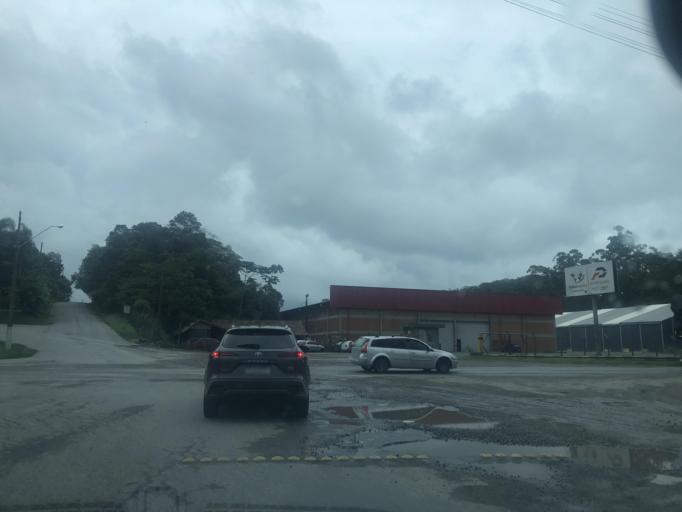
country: BR
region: Santa Catarina
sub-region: Sao Francisco Do Sul
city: Sao Francisco do Sul
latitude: -26.2404
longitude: -48.6176
